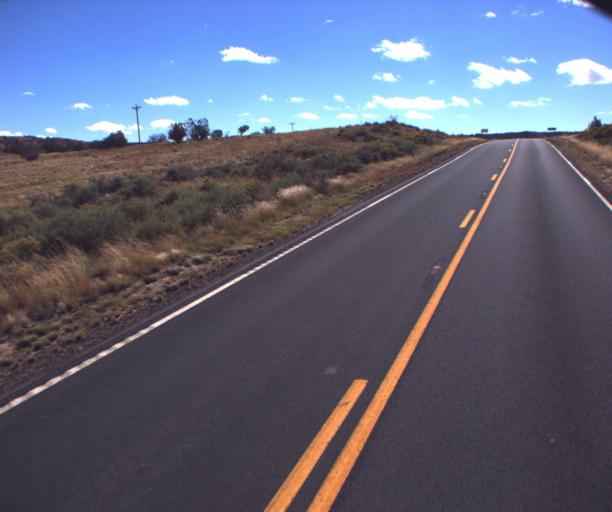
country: US
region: Arizona
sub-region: Apache County
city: Houck
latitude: 35.0510
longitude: -109.2746
